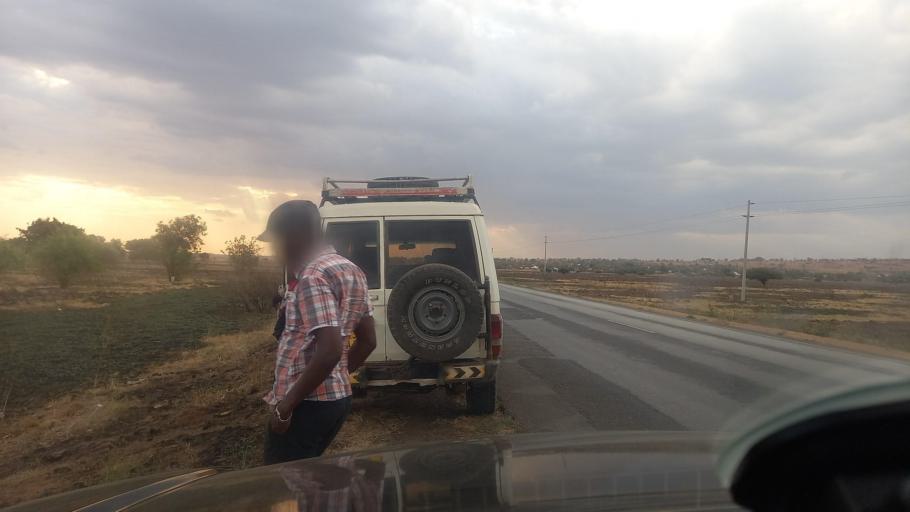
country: TZ
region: Dodoma
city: Kongwa
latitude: -6.0835
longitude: 36.5978
